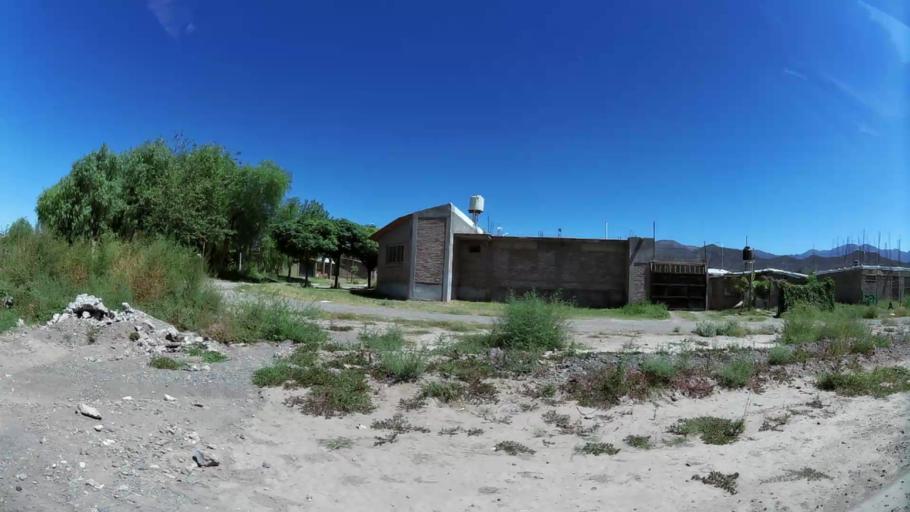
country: AR
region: Mendoza
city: Las Heras
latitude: -32.8427
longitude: -68.8621
